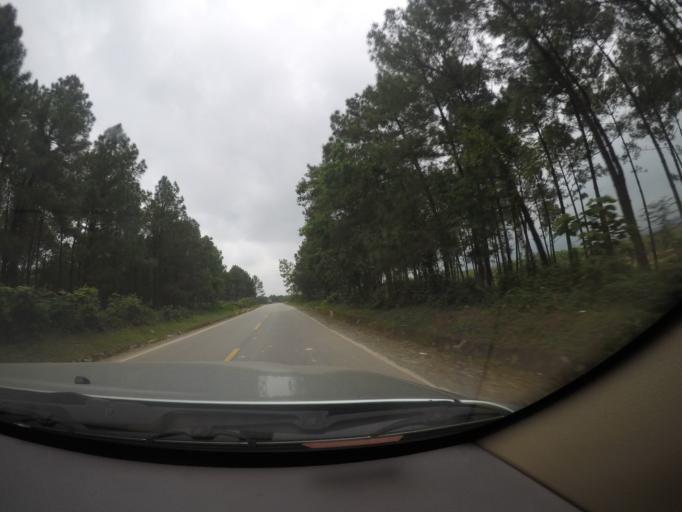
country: VN
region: Quang Binh
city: Kien Giang
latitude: 17.1628
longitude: 106.7427
